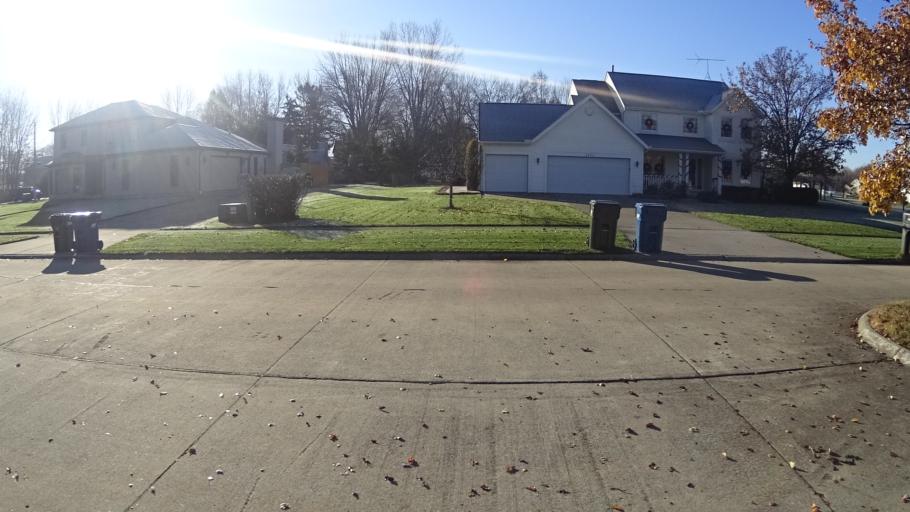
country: US
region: Ohio
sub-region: Lorain County
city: Sheffield
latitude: 41.4316
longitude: -82.0775
